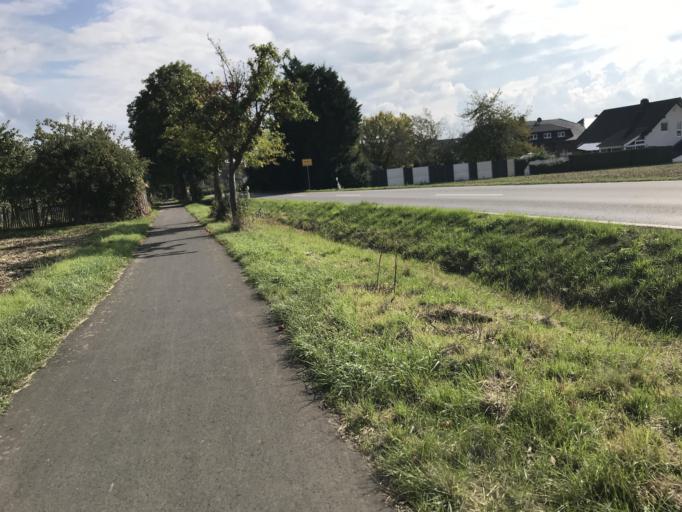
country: DE
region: Hesse
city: Gudensberg
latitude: 51.1679
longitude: 9.3724
